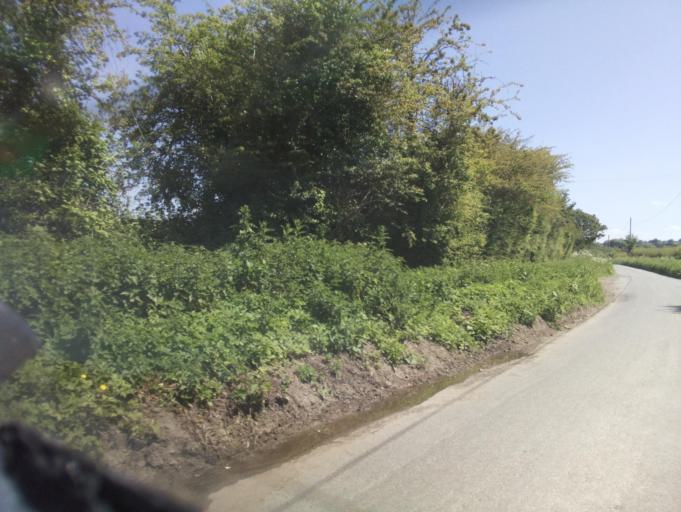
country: GB
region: England
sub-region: Wiltshire
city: Bremhill
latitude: 51.4525
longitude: -2.0675
